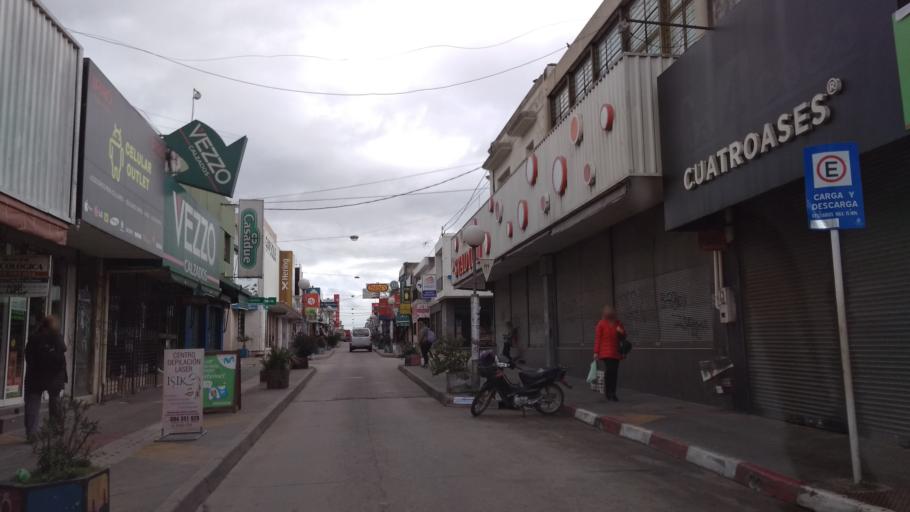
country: UY
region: Canelones
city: Pando
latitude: -34.7200
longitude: -55.9606
